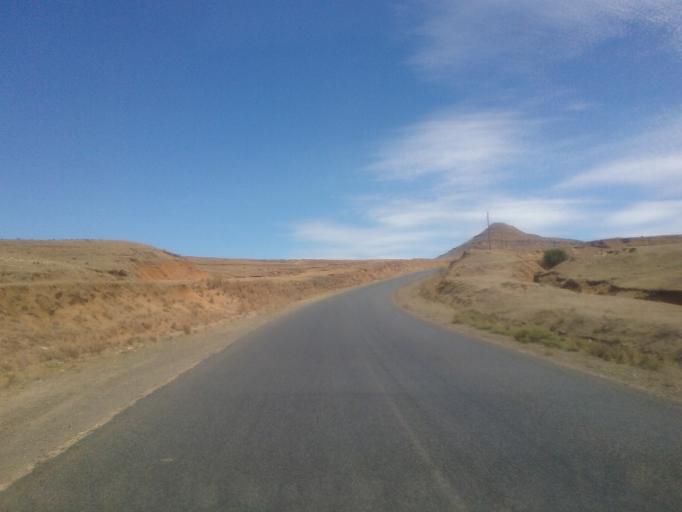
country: LS
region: Mohale's Hoek District
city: Mohale's Hoek
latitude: -30.0896
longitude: 27.4325
